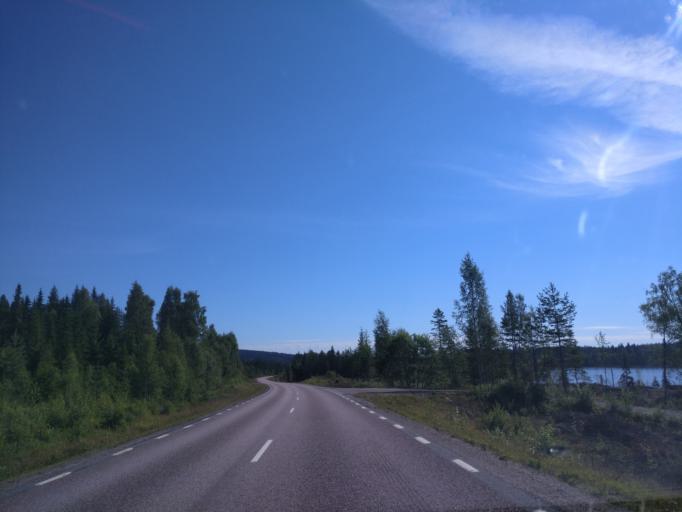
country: SE
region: Vaermland
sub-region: Filipstads Kommun
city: Lesjofors
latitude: 60.0478
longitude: 14.0052
